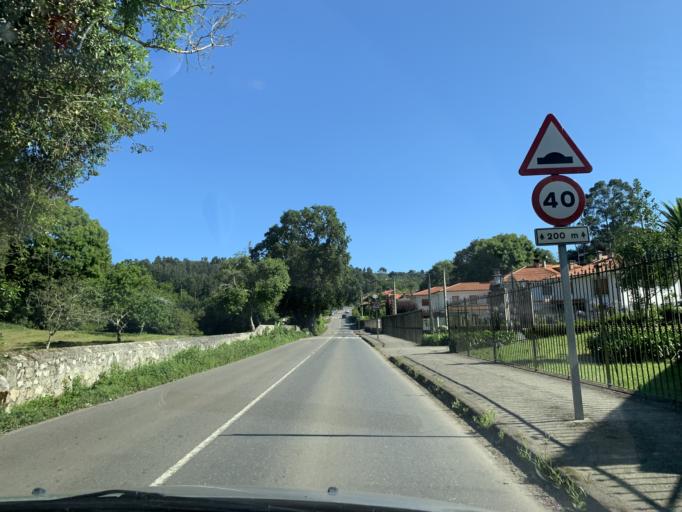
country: ES
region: Asturias
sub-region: Province of Asturias
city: Llanes
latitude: 43.4290
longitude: -4.8623
